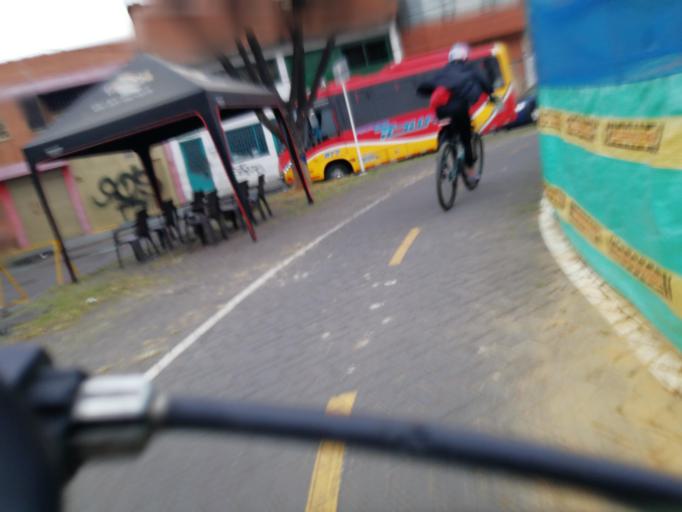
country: CO
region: Bogota D.C.
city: Bogota
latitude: 4.6117
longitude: -74.1414
